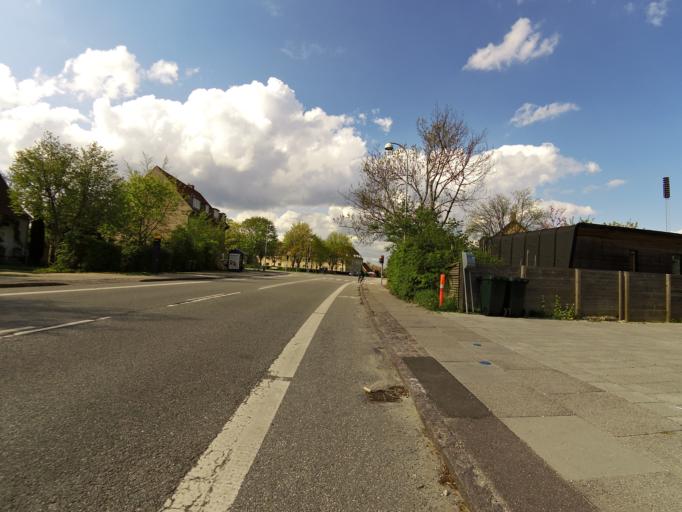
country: DK
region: Capital Region
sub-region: Gladsaxe Municipality
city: Buddinge
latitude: 55.7225
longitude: 12.5109
